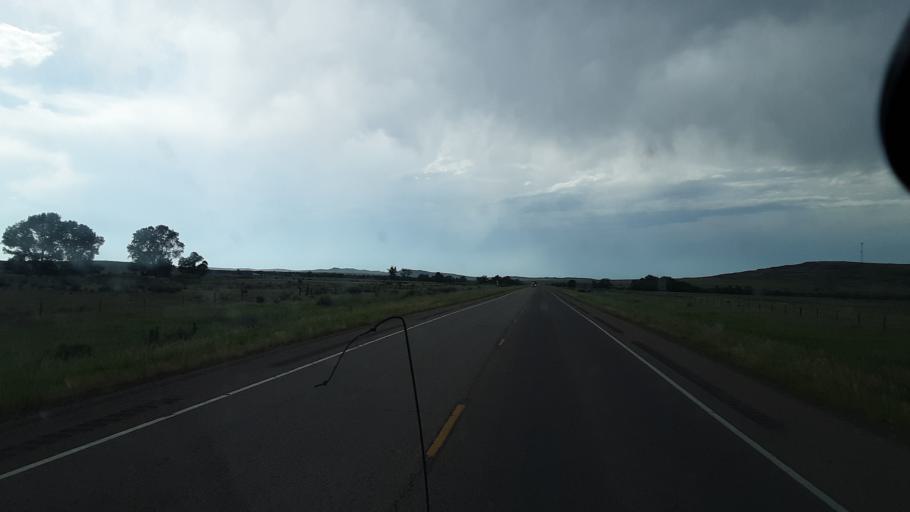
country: US
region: Wyoming
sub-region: Crook County
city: Sundance
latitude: 45.0425
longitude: -104.4410
